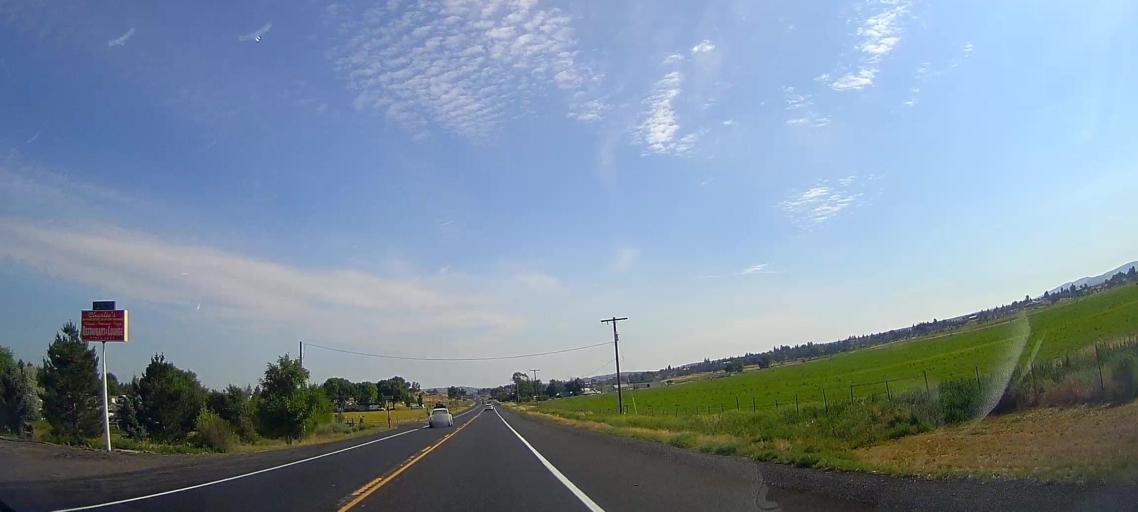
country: US
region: Oregon
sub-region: Jefferson County
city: Madras
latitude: 44.5968
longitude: -121.1451
